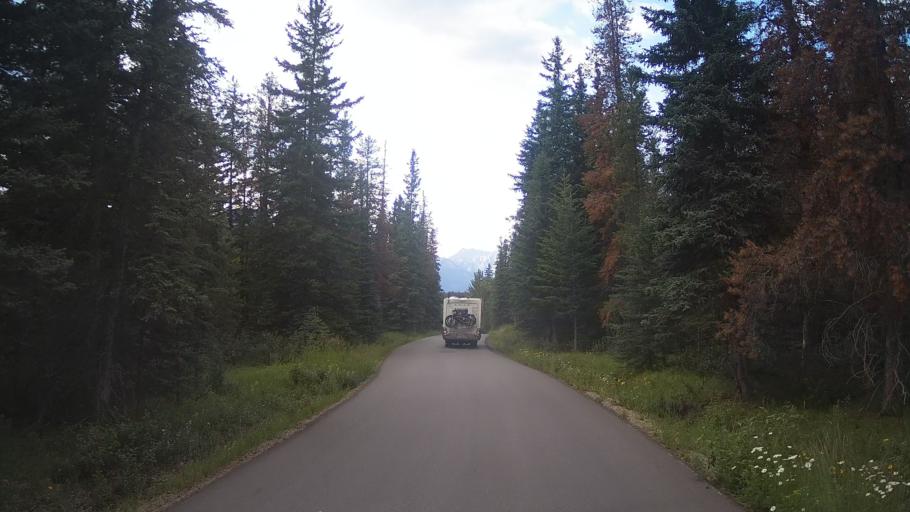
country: CA
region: Alberta
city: Jasper Park Lodge
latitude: 52.9308
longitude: -118.0317
